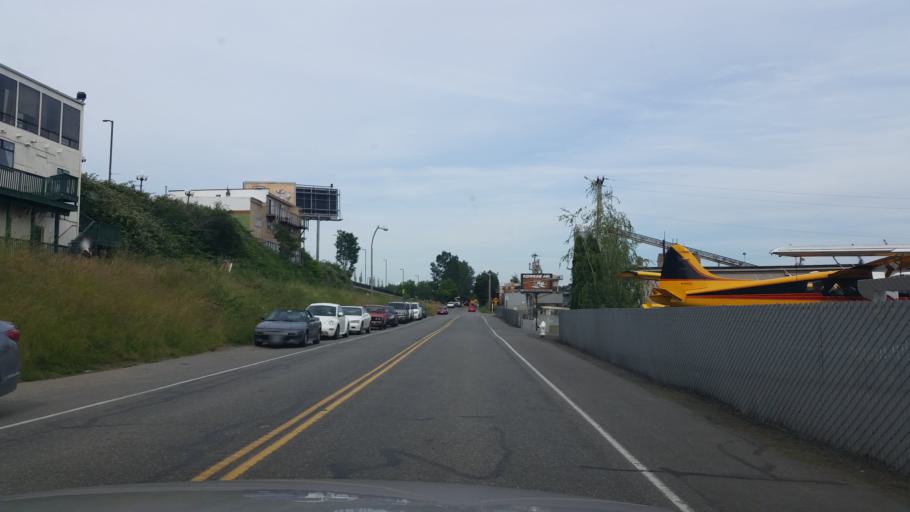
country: US
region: Washington
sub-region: King County
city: Kenmore
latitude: 47.7580
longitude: -122.2587
